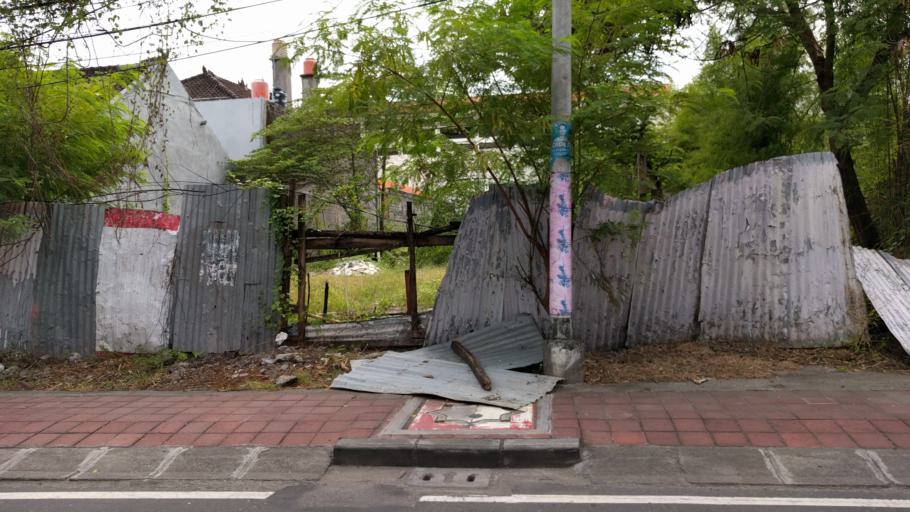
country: ID
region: Bali
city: Kuta
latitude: -8.6816
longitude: 115.1673
